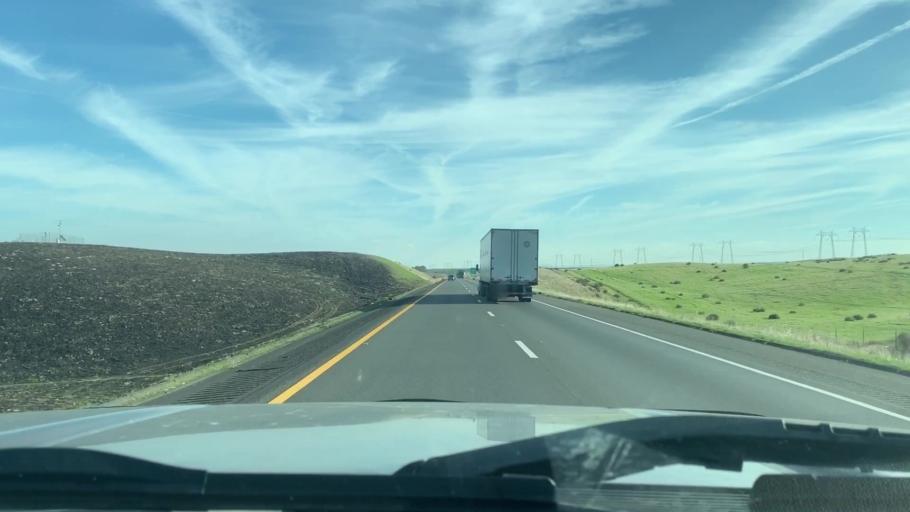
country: US
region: California
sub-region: Fresno County
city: Coalinga
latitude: 36.3049
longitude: -120.2784
